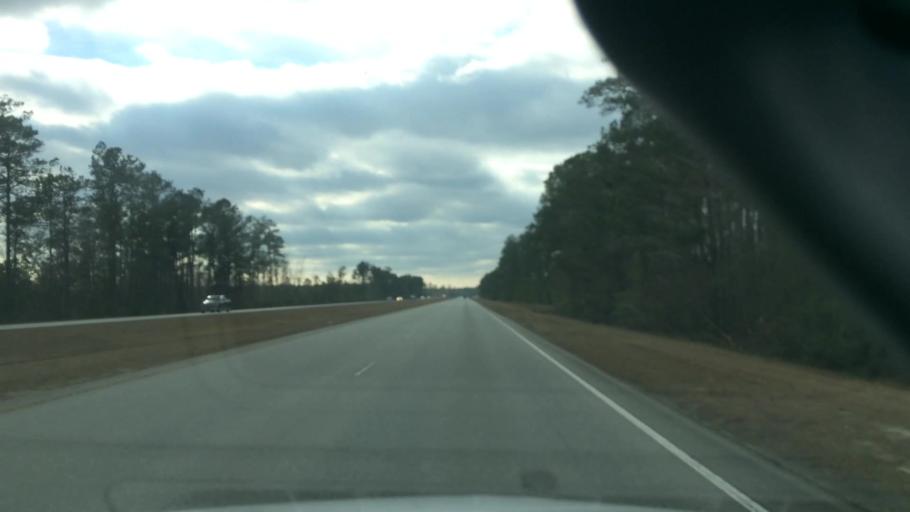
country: US
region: North Carolina
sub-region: Brunswick County
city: Bolivia
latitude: 34.0586
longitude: -78.2072
